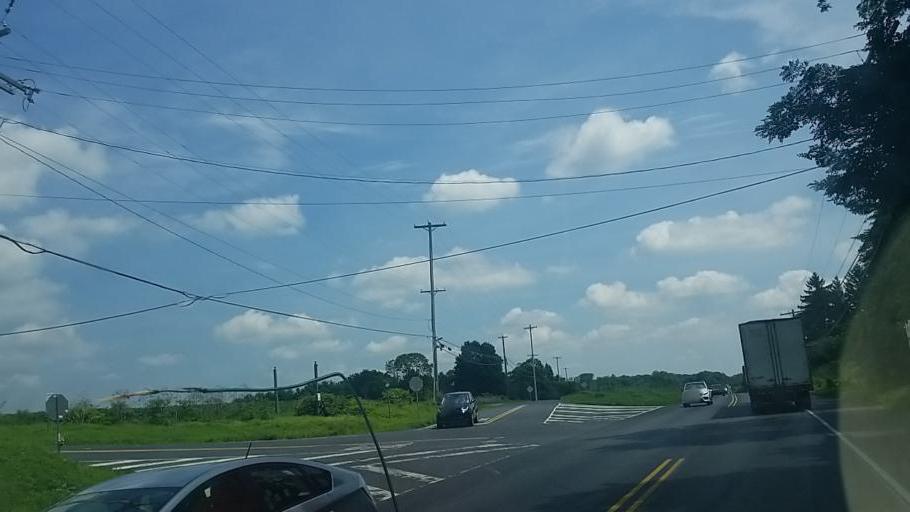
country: US
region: Pennsylvania
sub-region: Chester County
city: Toughkenamon
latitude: 39.8016
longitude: -75.7376
